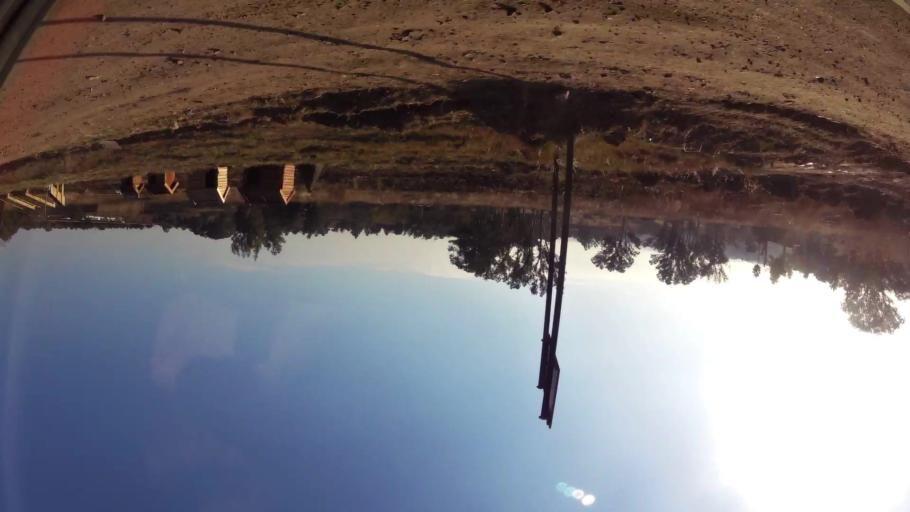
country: ZA
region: Gauteng
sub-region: West Rand District Municipality
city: Muldersdriseloop
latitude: -26.0055
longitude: 27.9102
